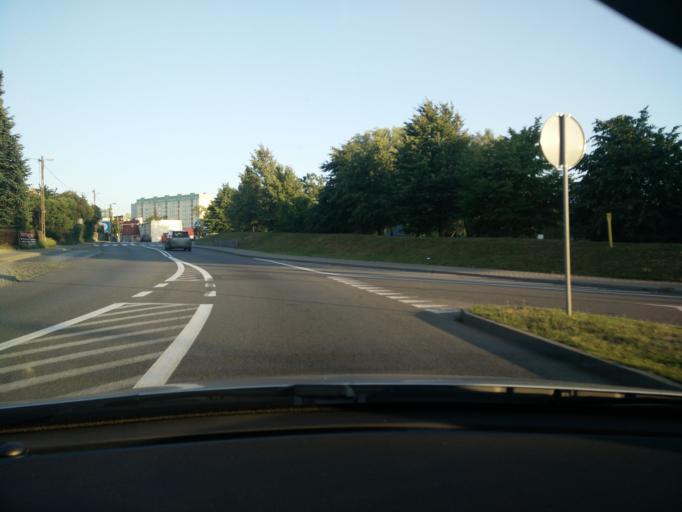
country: PL
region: Pomeranian Voivodeship
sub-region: Gdynia
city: Pogorze
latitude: 54.5609
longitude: 18.5096
